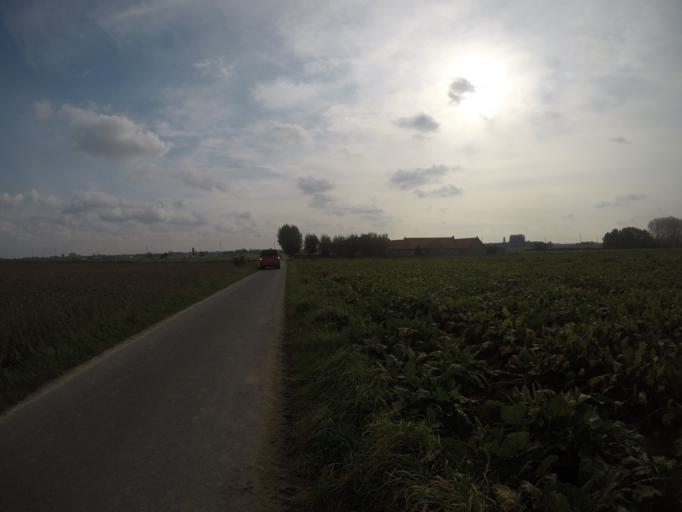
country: BE
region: Flanders
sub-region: Provincie West-Vlaanderen
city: Ledegem
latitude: 50.8389
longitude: 3.0738
